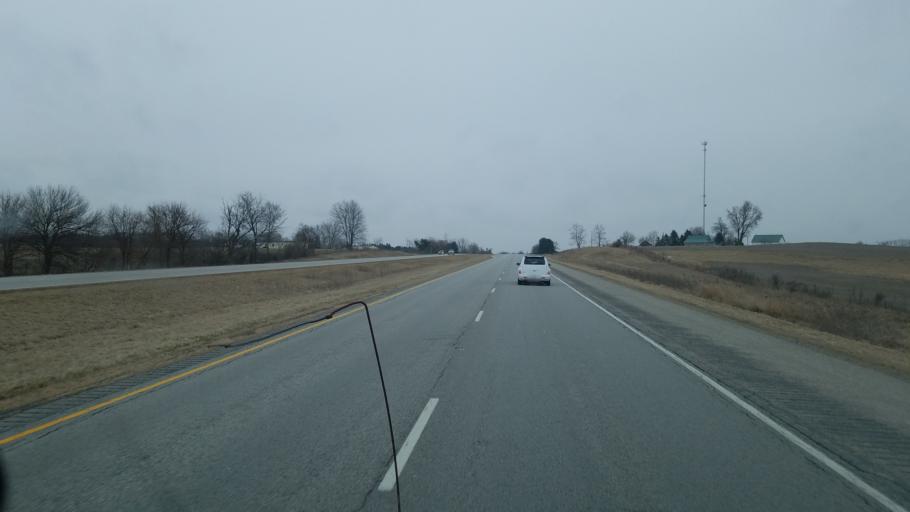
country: US
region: Indiana
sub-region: Miami County
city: Peru
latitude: 40.8905
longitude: -86.1504
